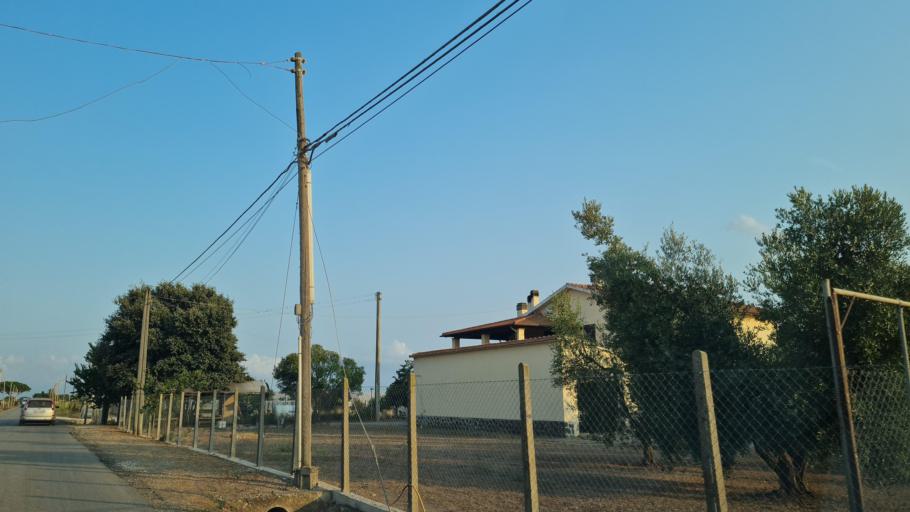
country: IT
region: Latium
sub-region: Provincia di Viterbo
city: Montalto di Castro
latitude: 42.3151
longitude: 11.6102
